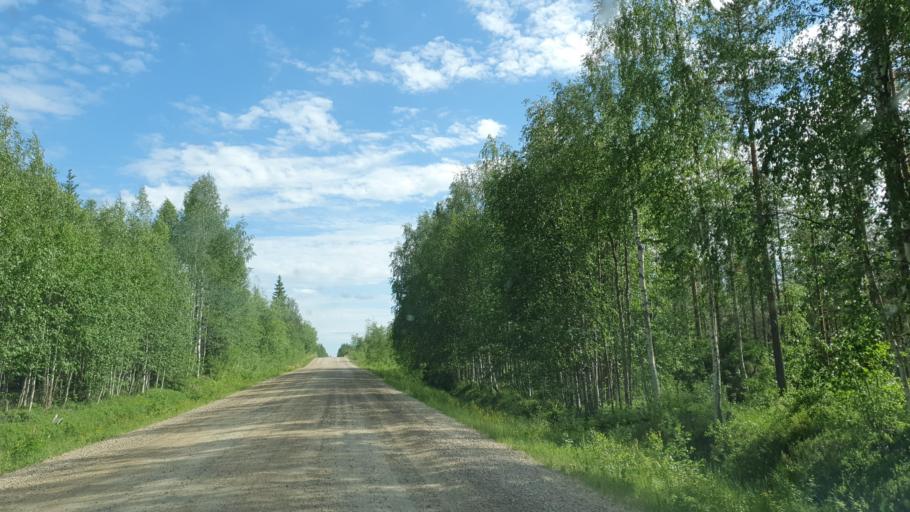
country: FI
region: Kainuu
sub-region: Kehys-Kainuu
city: Kuhmo
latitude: 64.4795
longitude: 29.5285
